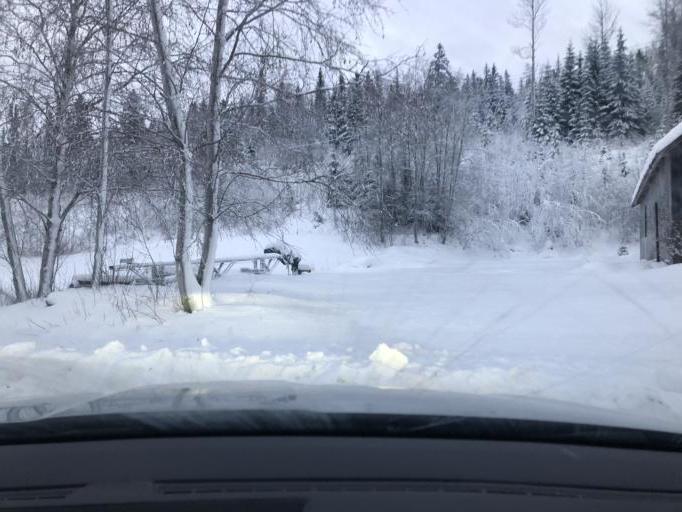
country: SE
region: Vaesternorrland
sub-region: Kramfors Kommun
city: Nordingra
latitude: 62.9063
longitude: 18.2413
